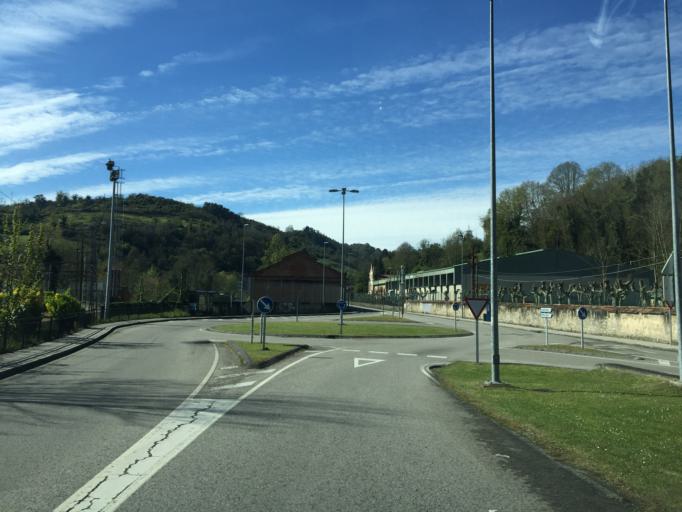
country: ES
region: Asturias
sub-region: Province of Asturias
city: Castandiello
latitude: 43.3513
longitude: -5.9684
